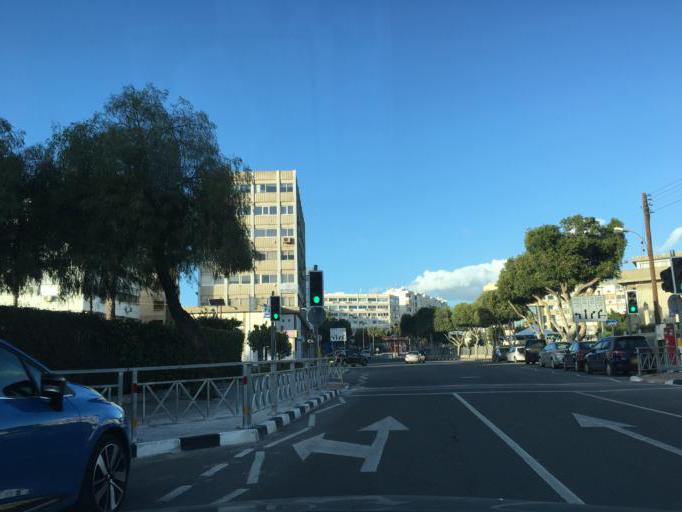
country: CY
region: Limassol
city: Limassol
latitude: 34.6851
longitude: 33.0529
